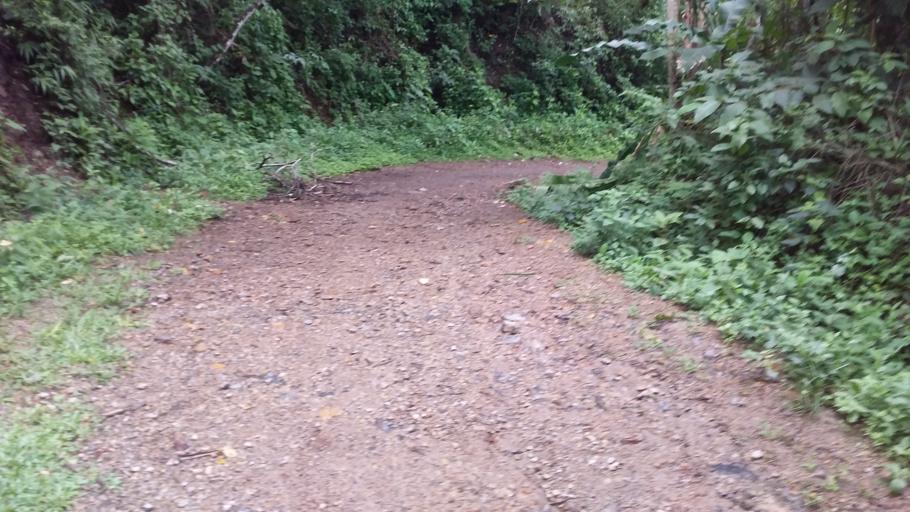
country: CO
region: Casanare
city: Nunchia
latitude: 5.6470
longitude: -72.2936
